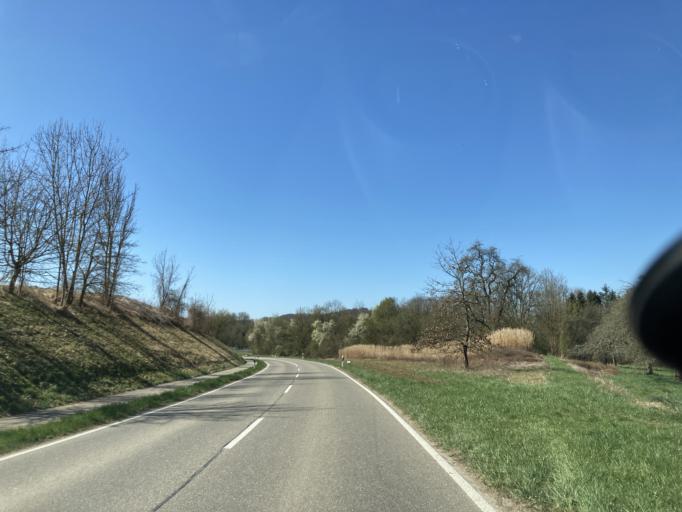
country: DE
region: Baden-Wuerttemberg
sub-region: Freiburg Region
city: Auggen
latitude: 47.7494
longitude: 7.6137
